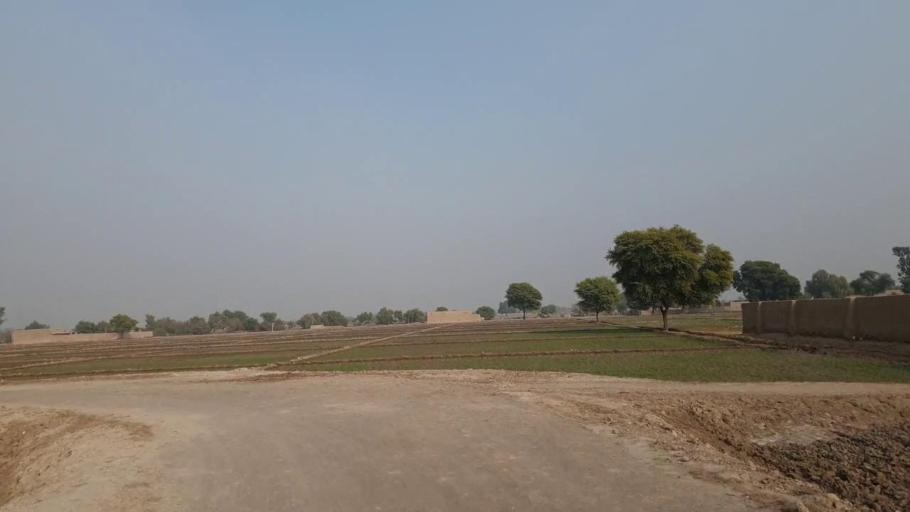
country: PK
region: Sindh
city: Bhan
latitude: 26.4625
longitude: 67.7100
